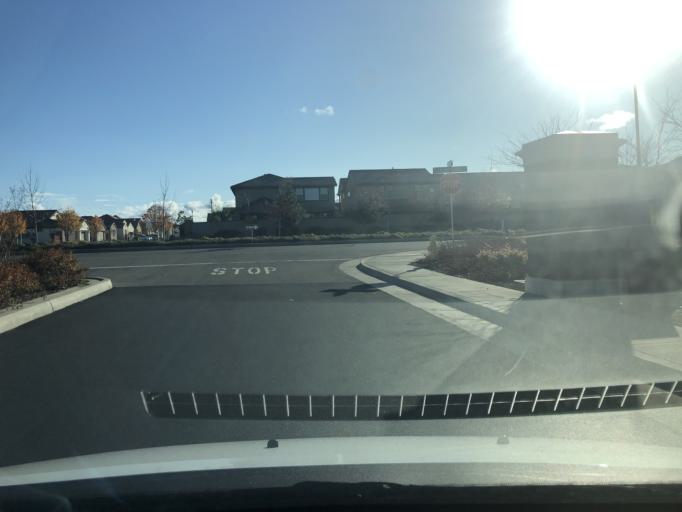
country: US
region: California
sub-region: Sacramento County
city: Antelope
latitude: 38.7758
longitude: -121.3830
